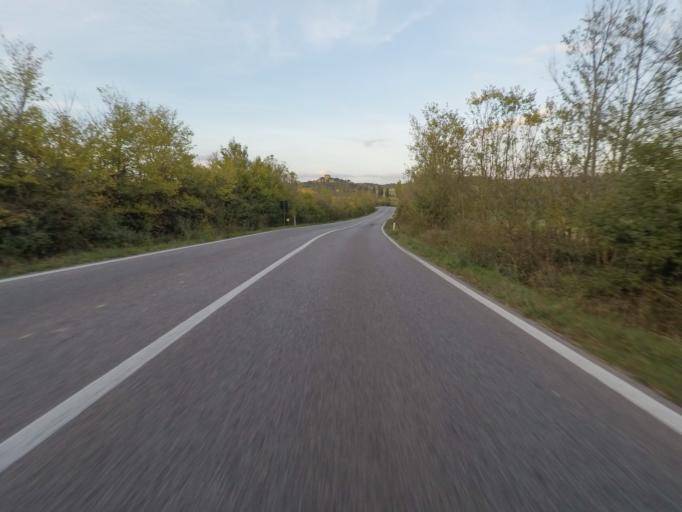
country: IT
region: Tuscany
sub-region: Provincia di Siena
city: Pienza
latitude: 43.0951
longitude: 11.6895
